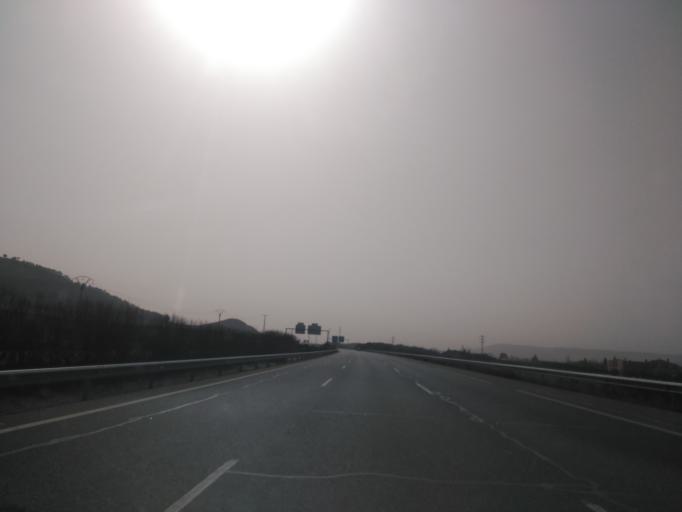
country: ES
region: Castille and Leon
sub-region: Provincia de Palencia
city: Palencia
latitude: 41.9969
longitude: -4.5028
